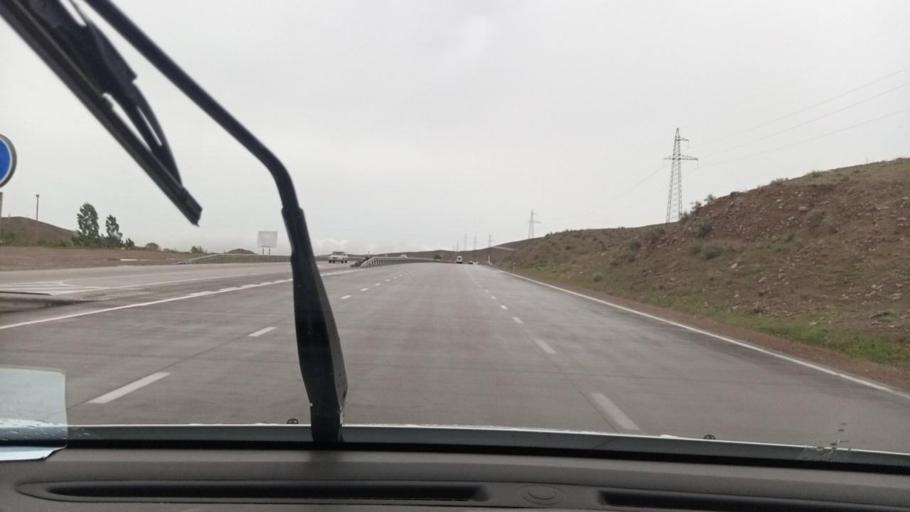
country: UZ
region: Namangan
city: Pop Shahri
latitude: 40.9410
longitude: 70.6898
